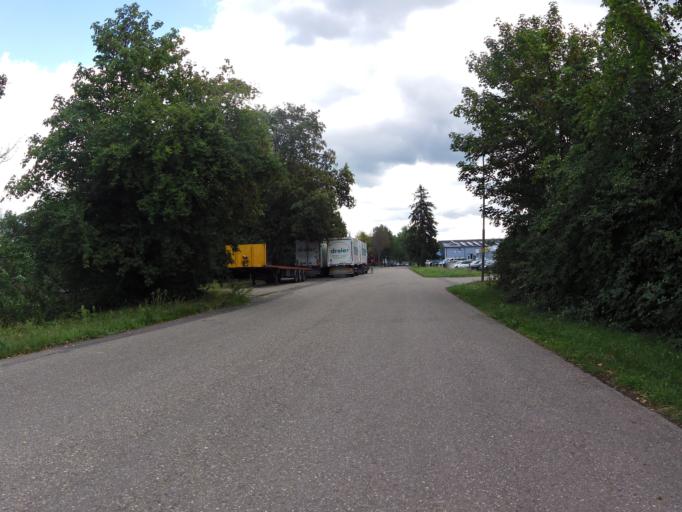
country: DE
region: Baden-Wuerttemberg
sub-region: Freiburg Region
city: Lahr
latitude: 48.3539
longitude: 7.8207
